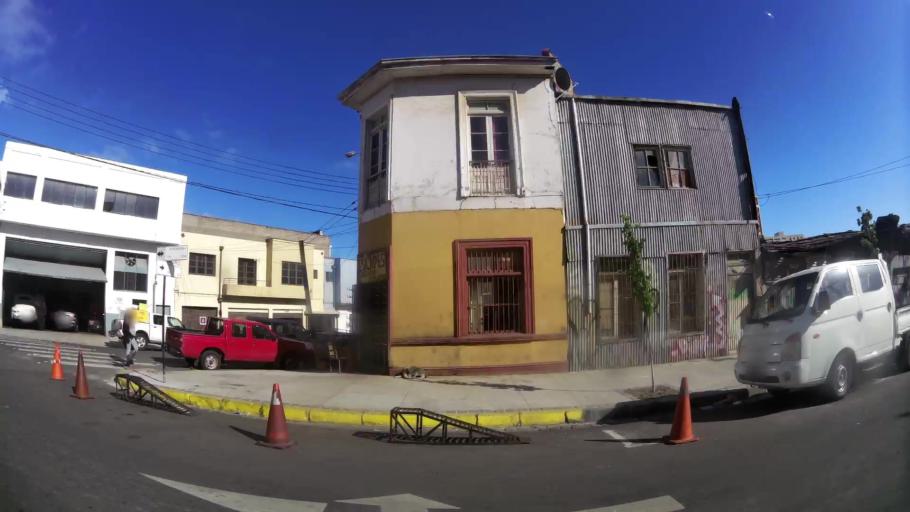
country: CL
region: Valparaiso
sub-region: Provincia de Valparaiso
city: Valparaiso
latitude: -33.0519
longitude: -71.6066
